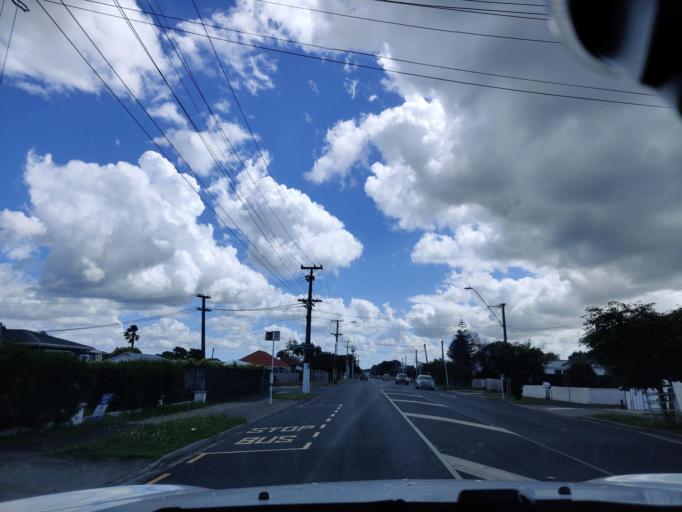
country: NZ
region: Auckland
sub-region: Auckland
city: Red Hill
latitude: -37.0553
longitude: 174.9583
